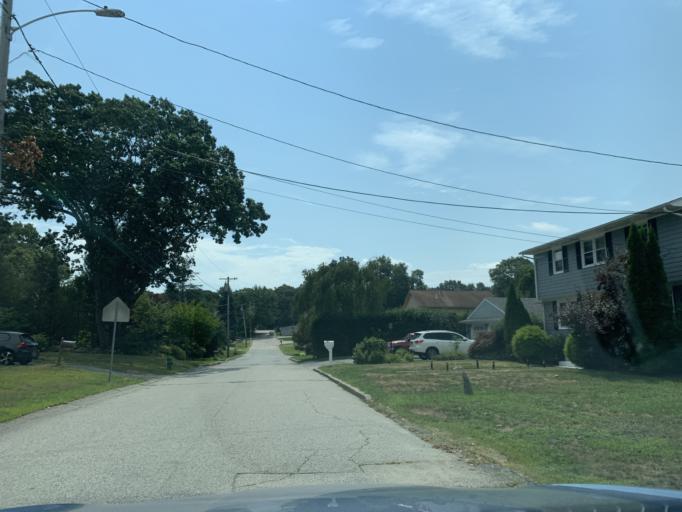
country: US
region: Rhode Island
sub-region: Providence County
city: Johnston
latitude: 41.7868
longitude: -71.4828
